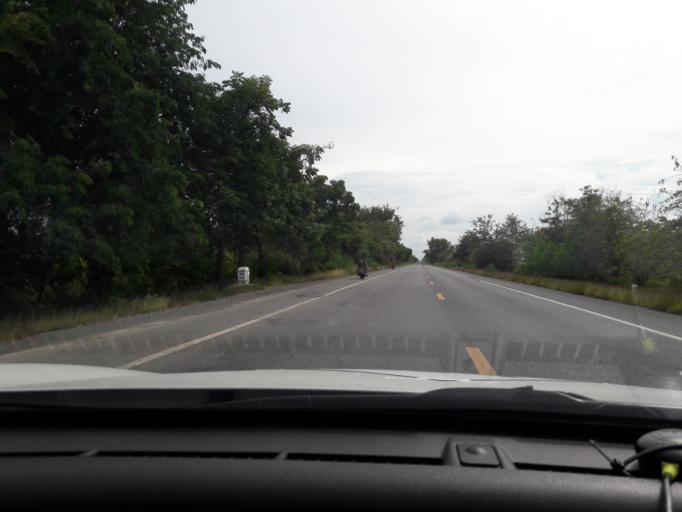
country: TH
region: Nakhon Sawan
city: Phai Sali
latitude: 15.5365
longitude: 100.5510
